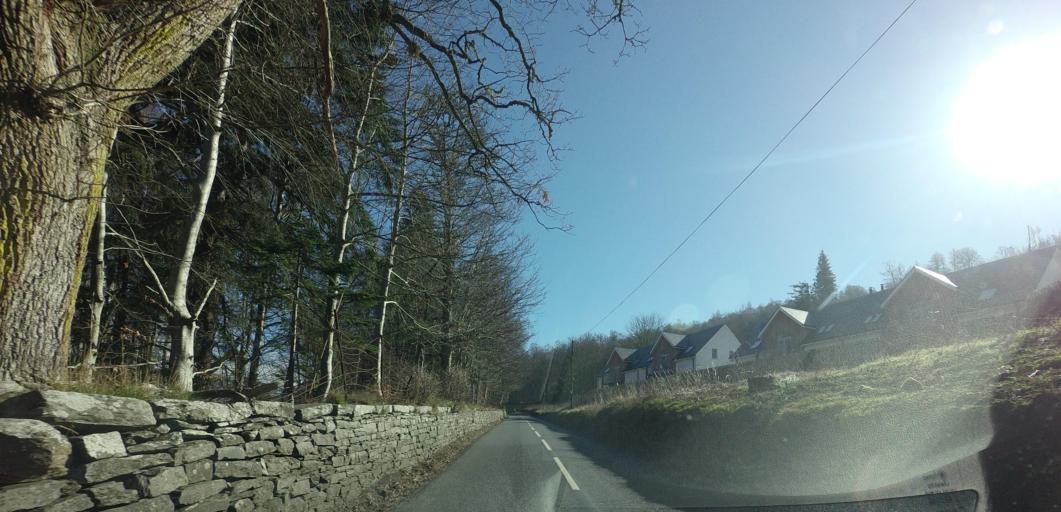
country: GB
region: Scotland
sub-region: Perth and Kinross
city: Aberfeldy
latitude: 56.5828
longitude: -3.9906
